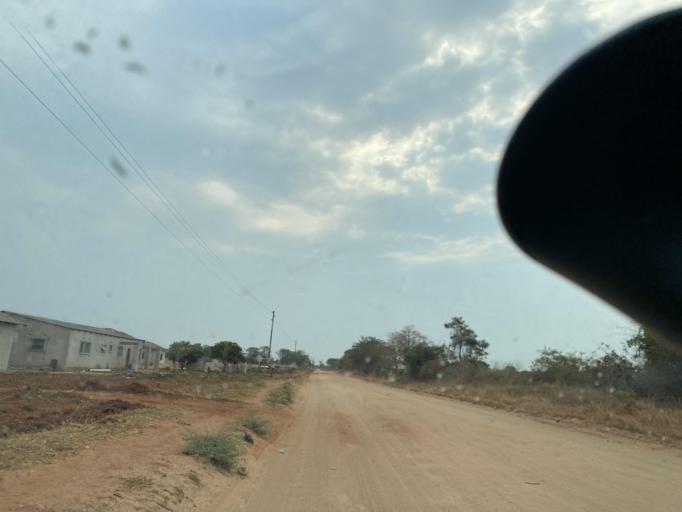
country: ZM
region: Lusaka
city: Lusaka
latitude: -15.2892
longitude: 28.2829
